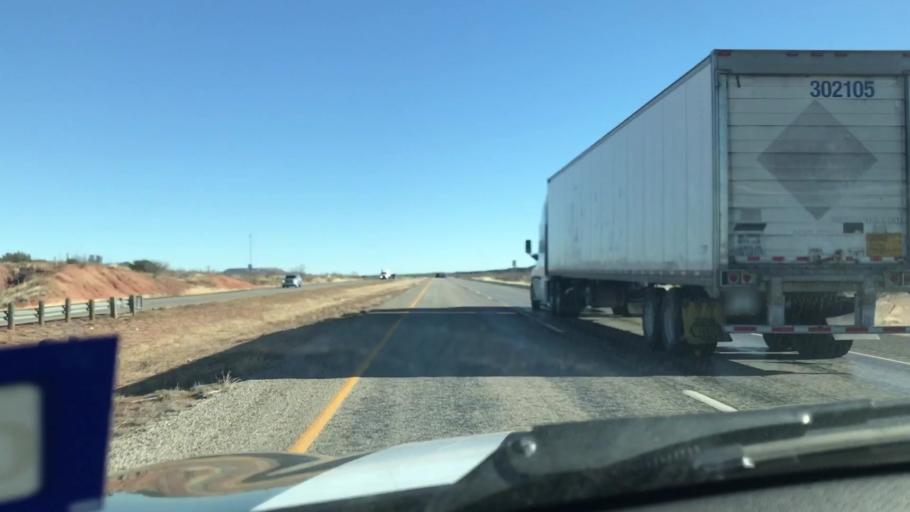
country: US
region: Texas
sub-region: Garza County
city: Post
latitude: 32.9931
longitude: -101.1463
